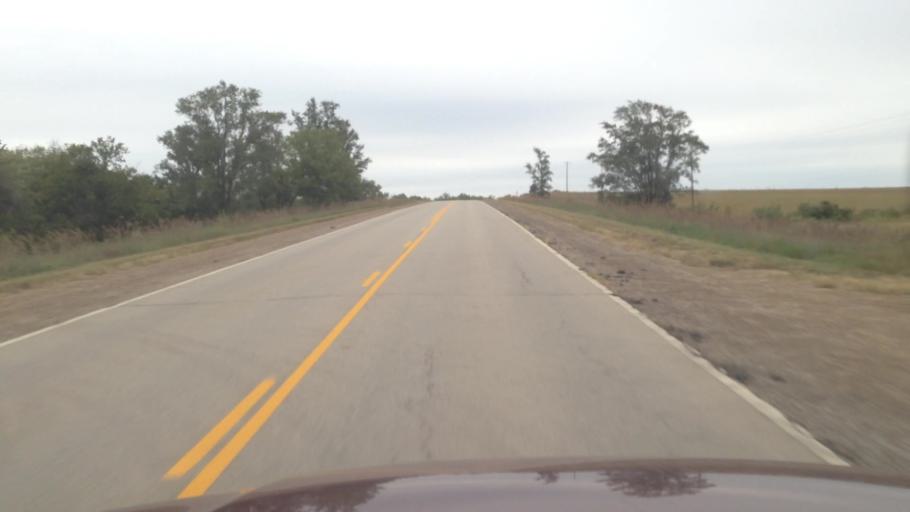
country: US
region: Kansas
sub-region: Jefferson County
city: Oskaloosa
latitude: 39.1152
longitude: -95.4837
